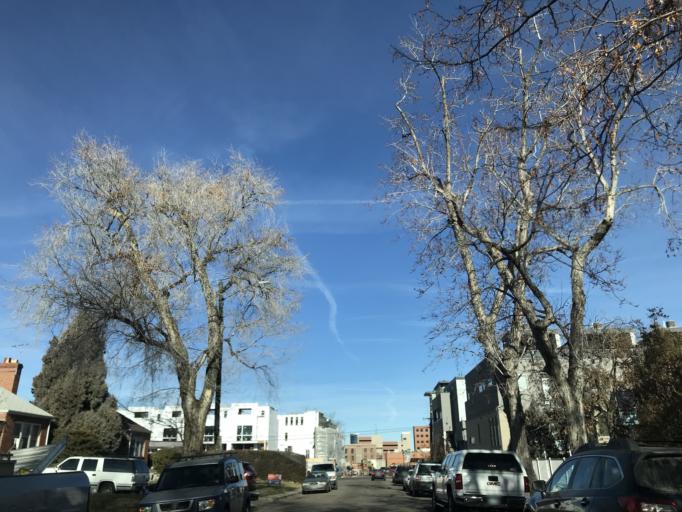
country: US
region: Colorado
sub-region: Arapahoe County
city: Glendale
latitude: 39.7284
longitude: -104.9371
